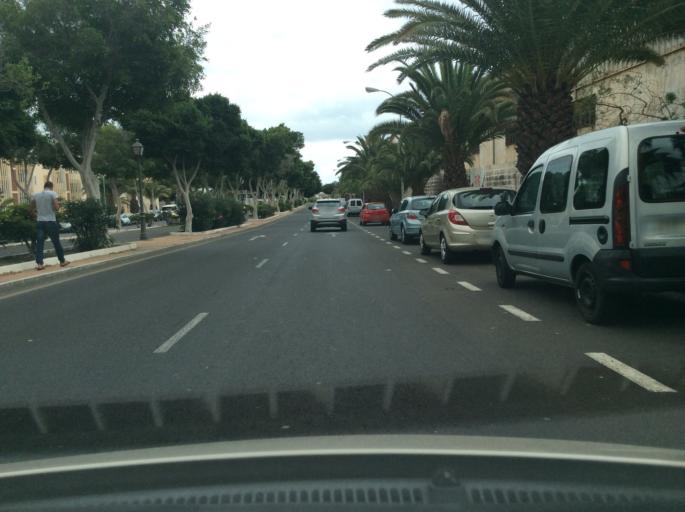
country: ES
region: Canary Islands
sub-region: Provincia de Las Palmas
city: Arrecife
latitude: 28.9687
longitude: -13.5463
